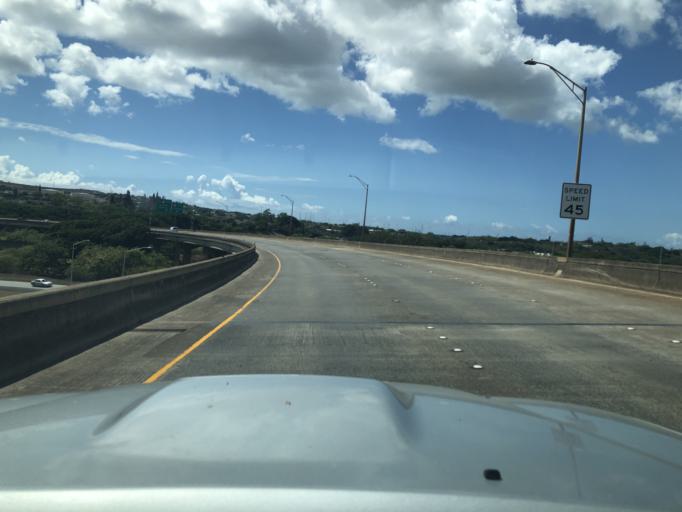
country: US
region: Hawaii
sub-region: Honolulu County
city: Halawa
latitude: 21.3734
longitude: -157.9270
